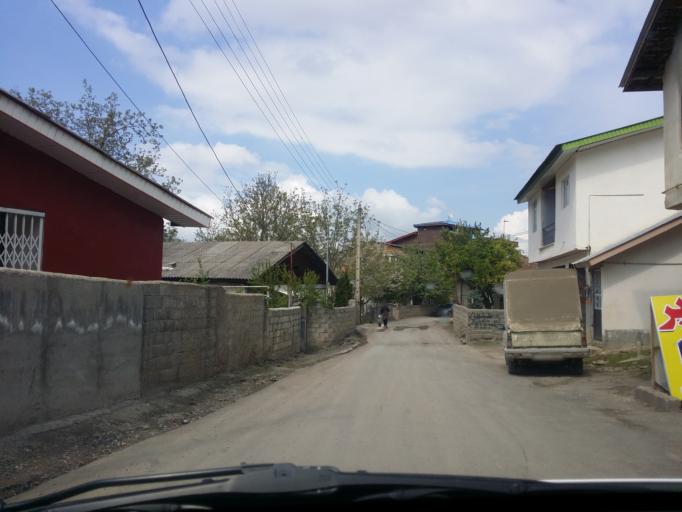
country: IR
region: Mazandaran
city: `Abbasabad
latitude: 36.4893
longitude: 51.1472
